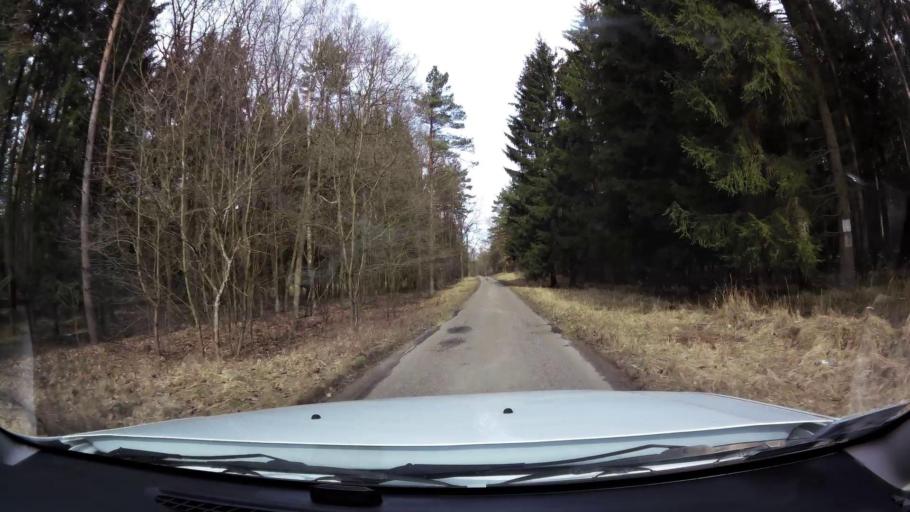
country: PL
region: West Pomeranian Voivodeship
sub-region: Powiat drawski
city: Drawsko Pomorskie
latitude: 53.4852
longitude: 15.7000
